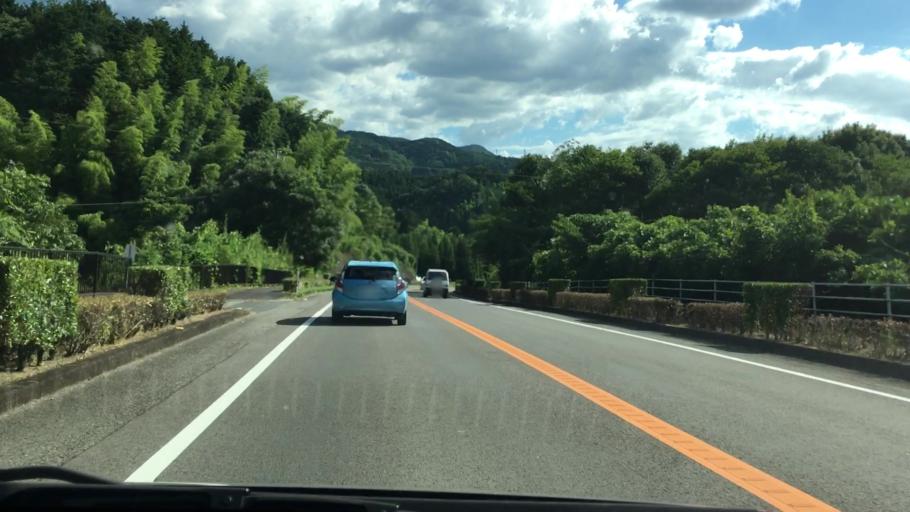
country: JP
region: Saga Prefecture
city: Takeocho-takeo
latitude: 33.1944
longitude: 129.9678
